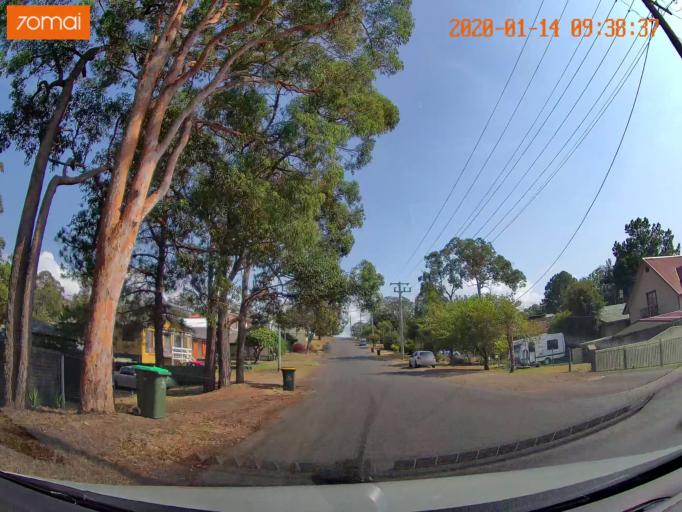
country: AU
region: New South Wales
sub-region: Lake Macquarie Shire
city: Arcadia vale
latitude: -33.1102
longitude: 151.5561
